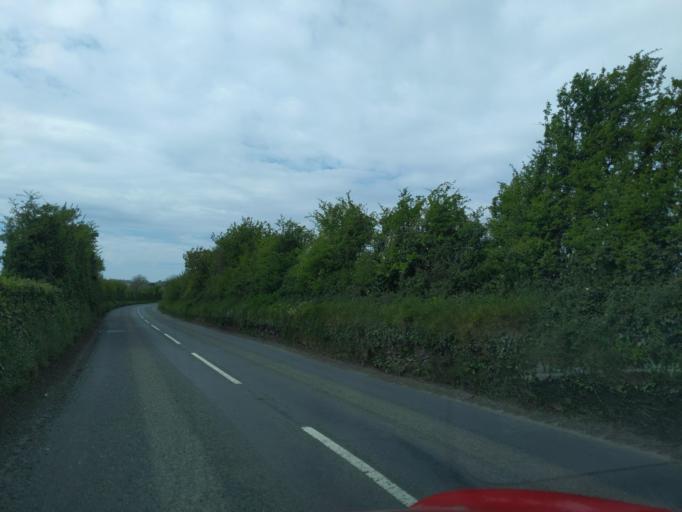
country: GB
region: England
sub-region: Cornwall
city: Wadebridge
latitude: 50.5364
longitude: -4.8503
